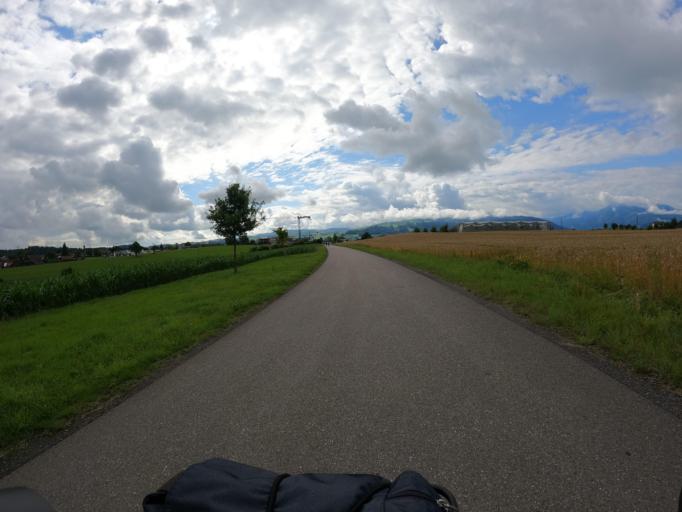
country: CH
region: Zug
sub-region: Zug
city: Steinhausen
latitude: 47.2004
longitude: 8.4737
